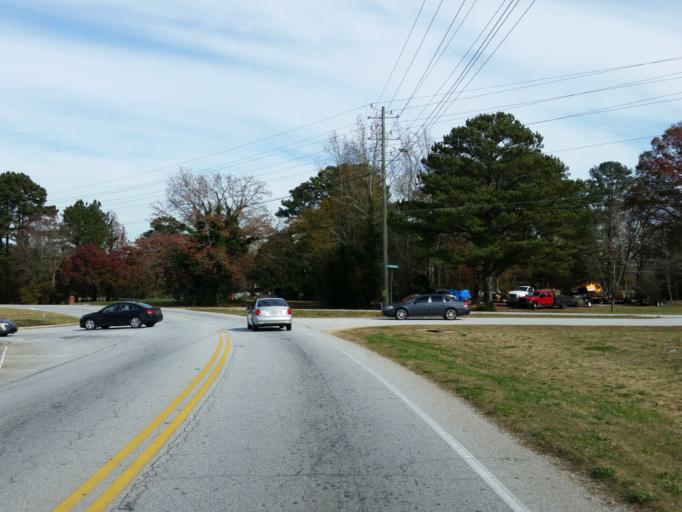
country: US
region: Georgia
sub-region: Douglas County
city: Lithia Springs
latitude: 33.7339
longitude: -84.6677
